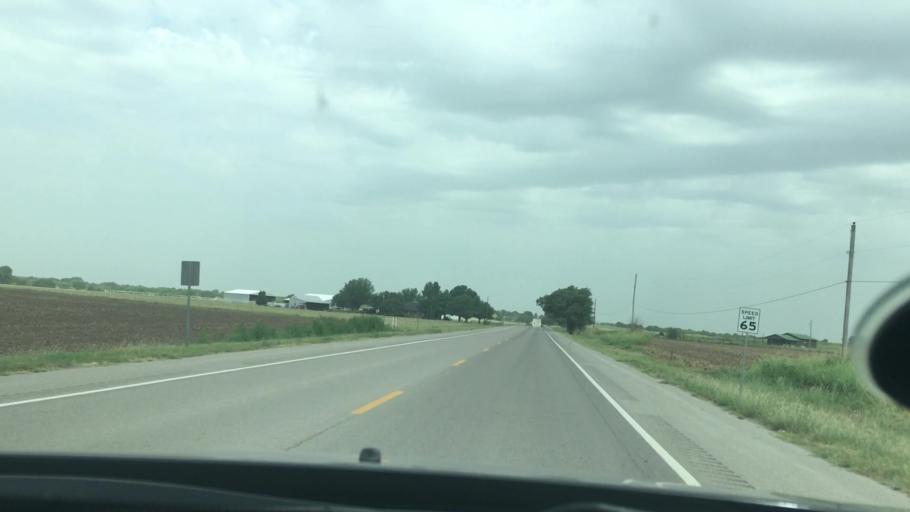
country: US
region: Oklahoma
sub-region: Garvin County
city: Pauls Valley
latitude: 34.8329
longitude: -97.2628
